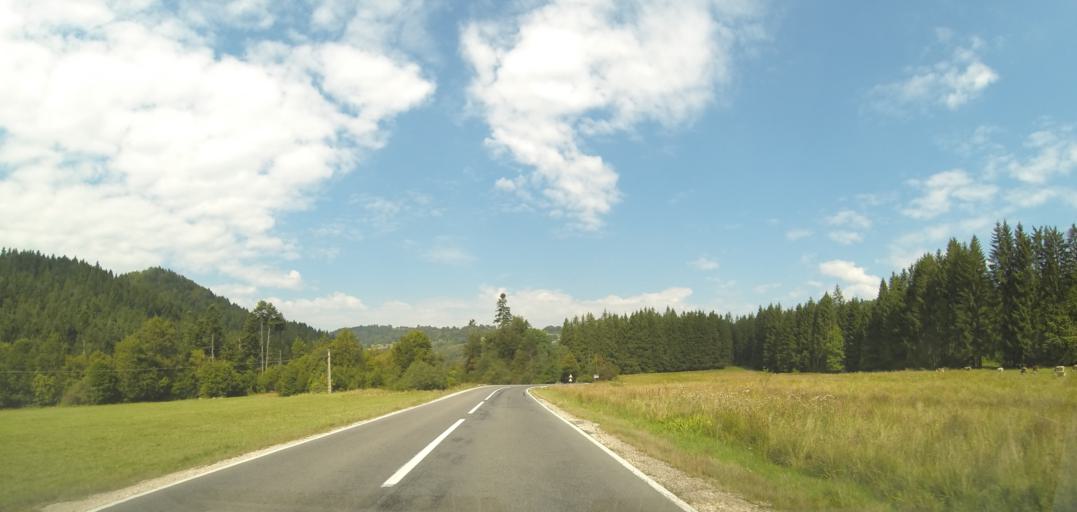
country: RO
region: Brasov
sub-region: Comuna Tarlungeni
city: Zizin
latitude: 45.5485
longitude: 25.8149
